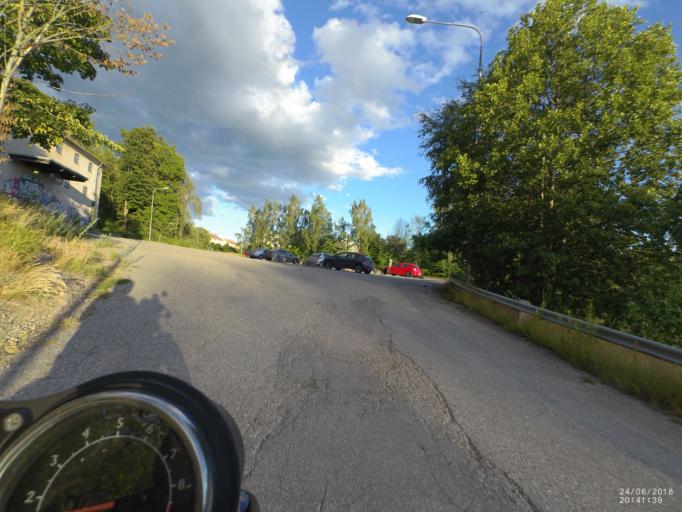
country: SE
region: Soedermanland
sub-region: Nykopings Kommun
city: Nykoping
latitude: 58.7590
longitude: 17.0070
